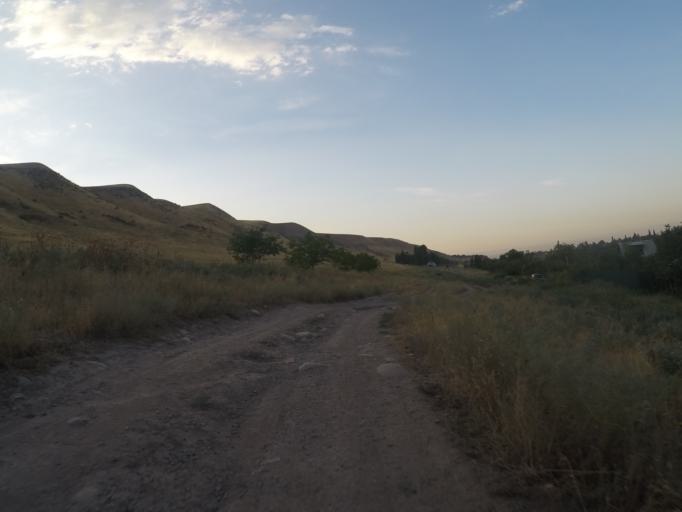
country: KG
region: Chuy
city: Bishkek
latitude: 42.7694
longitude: 74.6388
